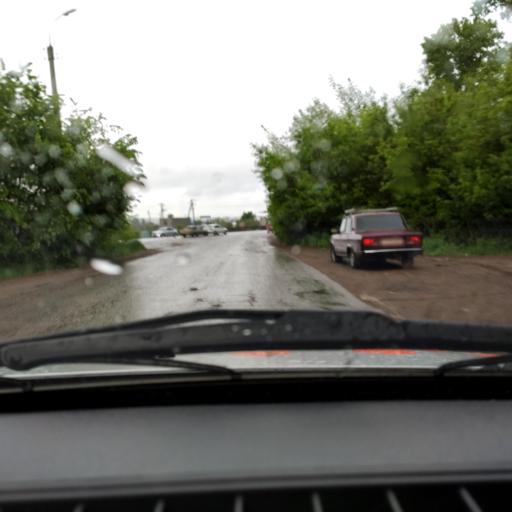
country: RU
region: Bashkortostan
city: Sterlitamak
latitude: 53.5947
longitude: 55.9146
